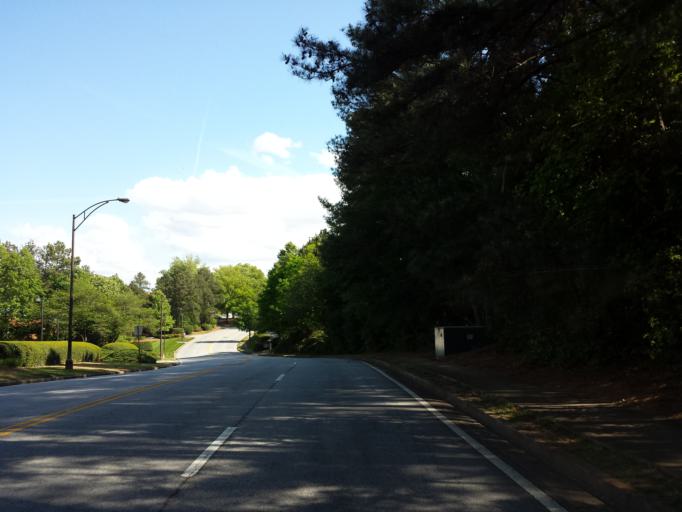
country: US
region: Georgia
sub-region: Cobb County
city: Smyrna
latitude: 33.9087
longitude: -84.4795
